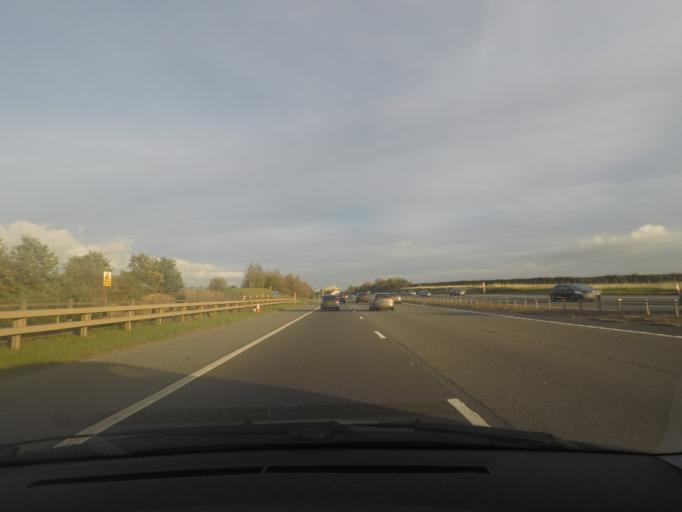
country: GB
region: England
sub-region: City and Borough of Leeds
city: Swillington
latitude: 53.7755
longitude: -1.4517
